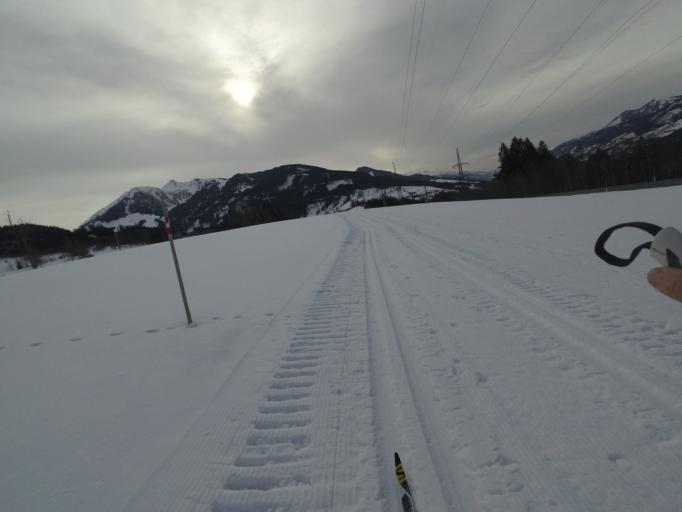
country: AT
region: Salzburg
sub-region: Politischer Bezirk Zell am See
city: Taxenbach
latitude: 47.2871
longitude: 12.9880
